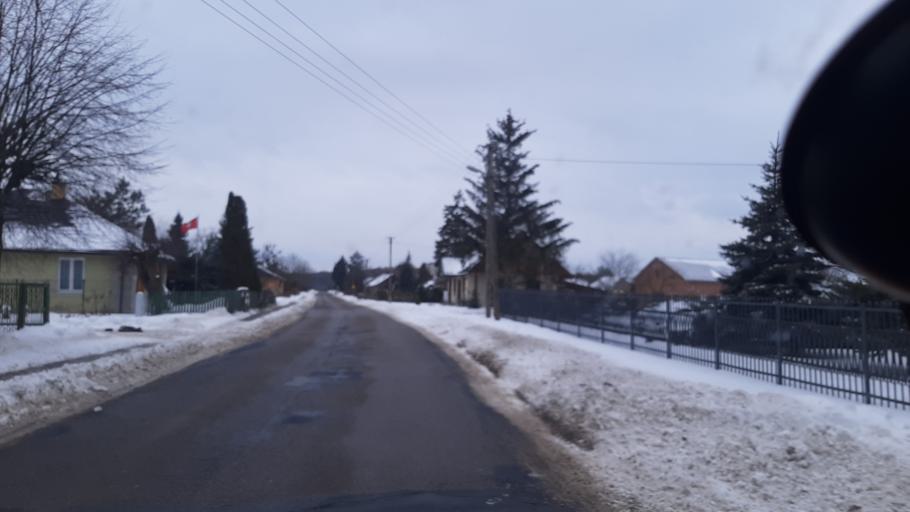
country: PL
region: Lublin Voivodeship
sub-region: Powiat pulawski
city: Kurow
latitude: 51.4342
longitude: 22.2300
